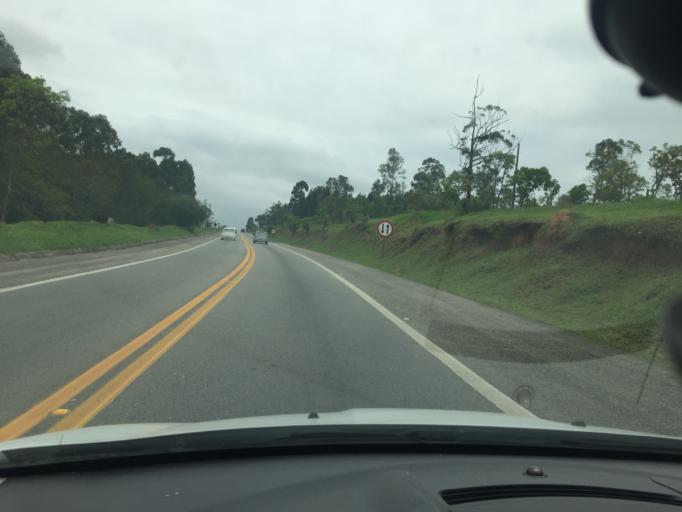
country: BR
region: Sao Paulo
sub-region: Jundiai
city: Jundiai
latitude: -23.1558
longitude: -46.8776
